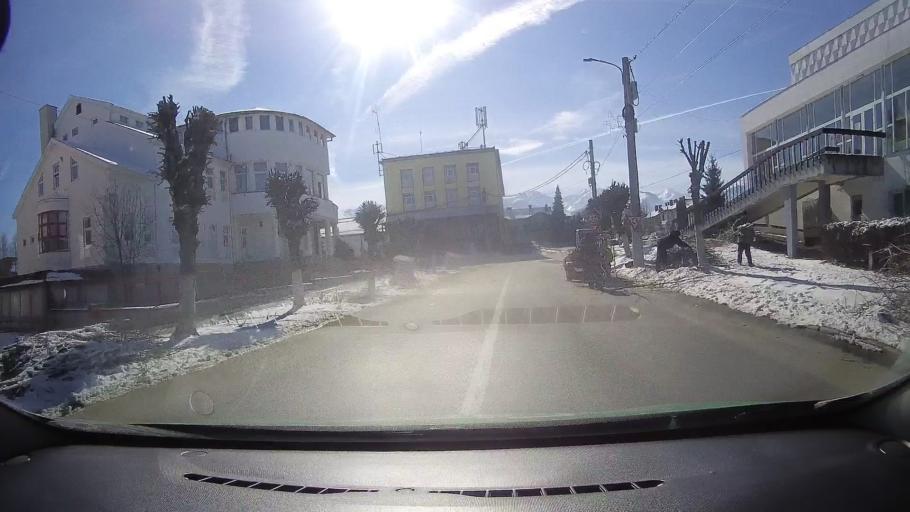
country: RO
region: Brasov
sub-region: Oras Victoria
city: Victoria
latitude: 45.7306
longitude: 24.7015
